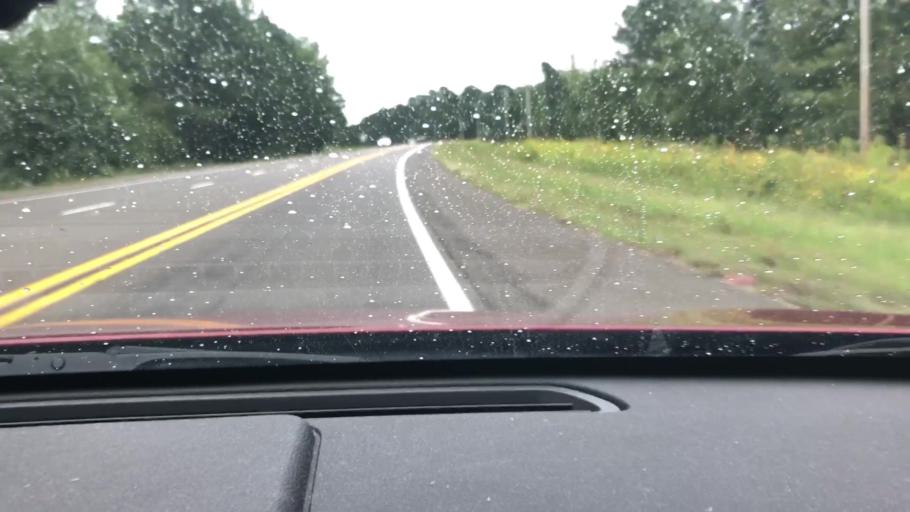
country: US
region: Arkansas
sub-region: Columbia County
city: Waldo
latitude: 33.3505
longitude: -93.3574
